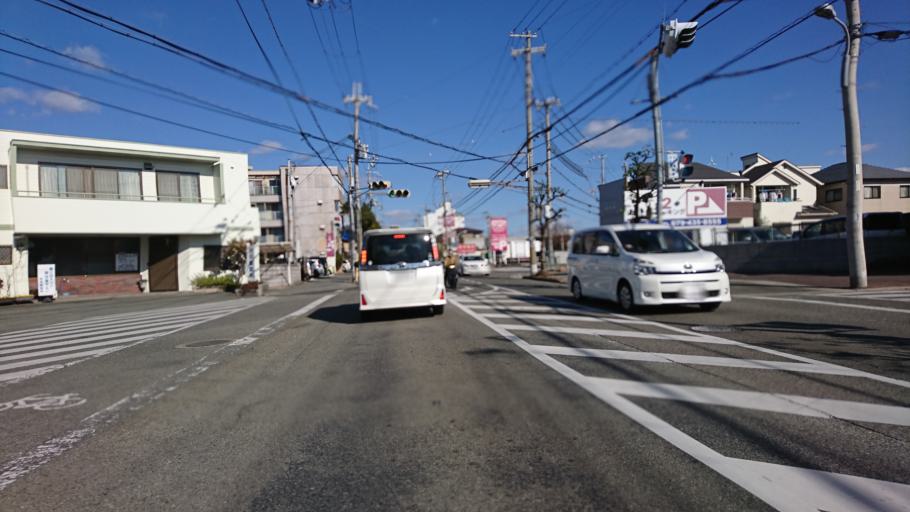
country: JP
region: Hyogo
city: Kakogawacho-honmachi
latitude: 34.7367
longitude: 134.8603
